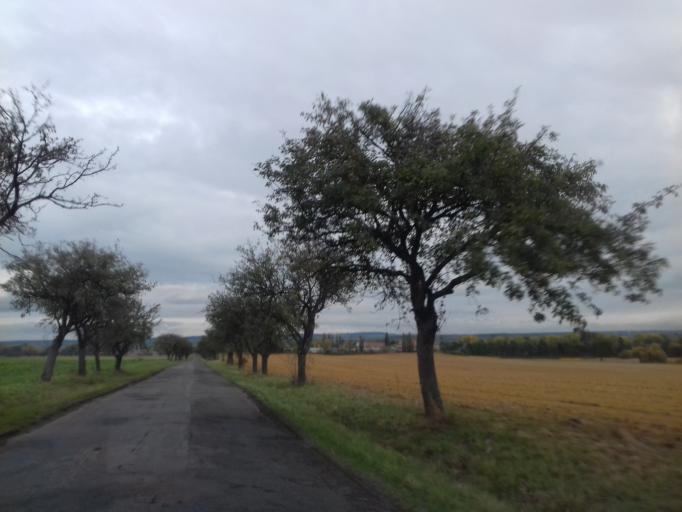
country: CZ
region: Pardubicky
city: Hrochuv Tynec
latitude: 49.9228
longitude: 15.8959
